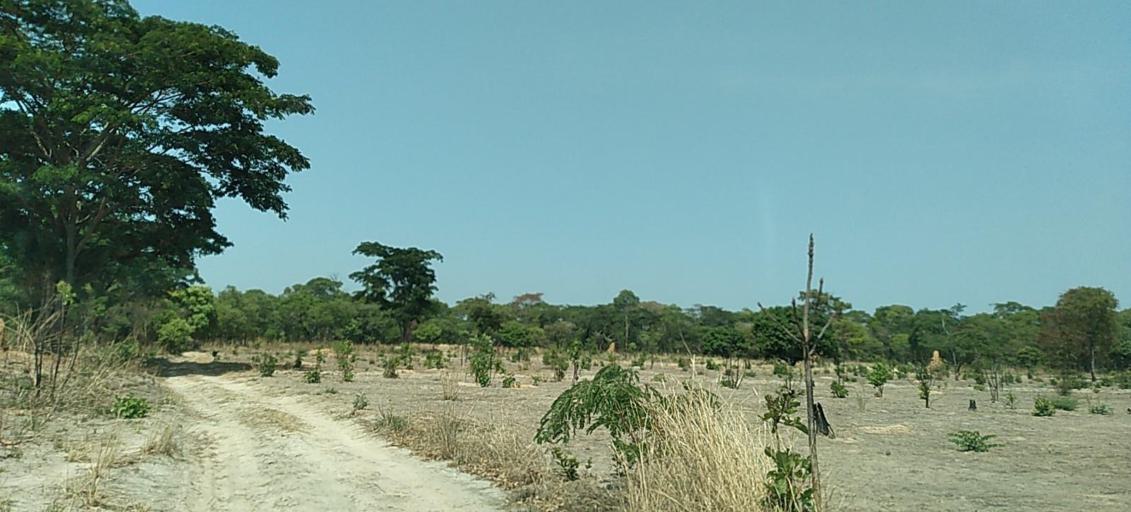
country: ZM
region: Copperbelt
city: Mpongwe
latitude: -13.7928
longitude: 28.0895
